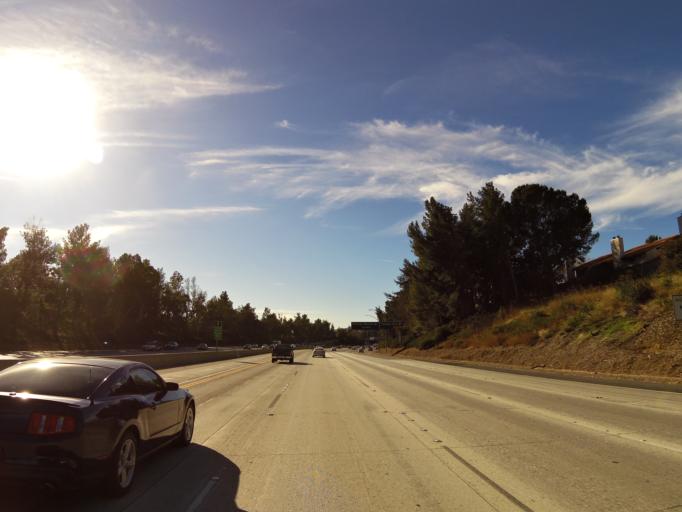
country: US
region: California
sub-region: Los Angeles County
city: Northridge
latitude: 34.2732
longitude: -118.5504
